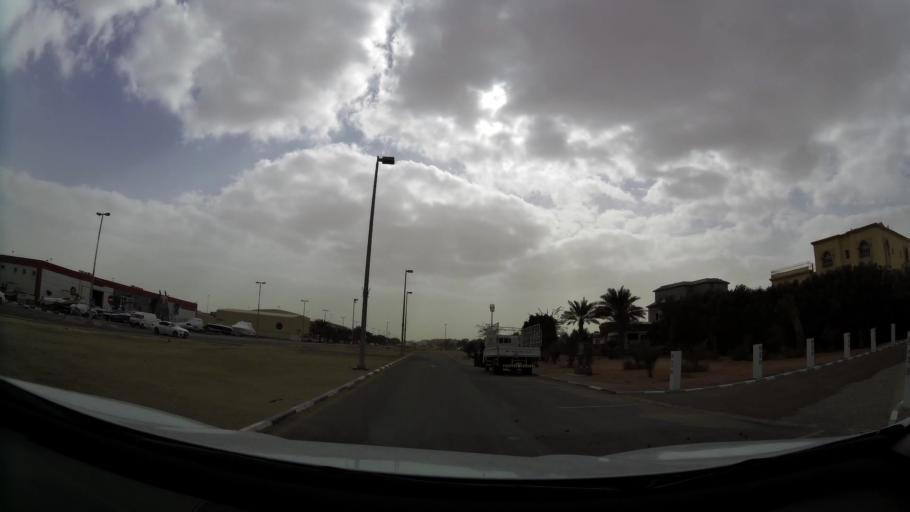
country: AE
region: Abu Dhabi
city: Abu Dhabi
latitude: 24.4151
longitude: 54.4965
